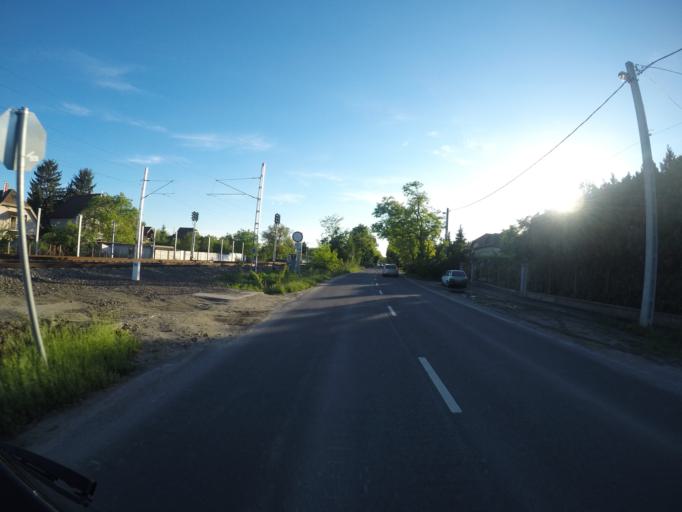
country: HU
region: Budapest
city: Budapest XVII. keruelet
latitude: 47.4885
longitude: 19.2750
